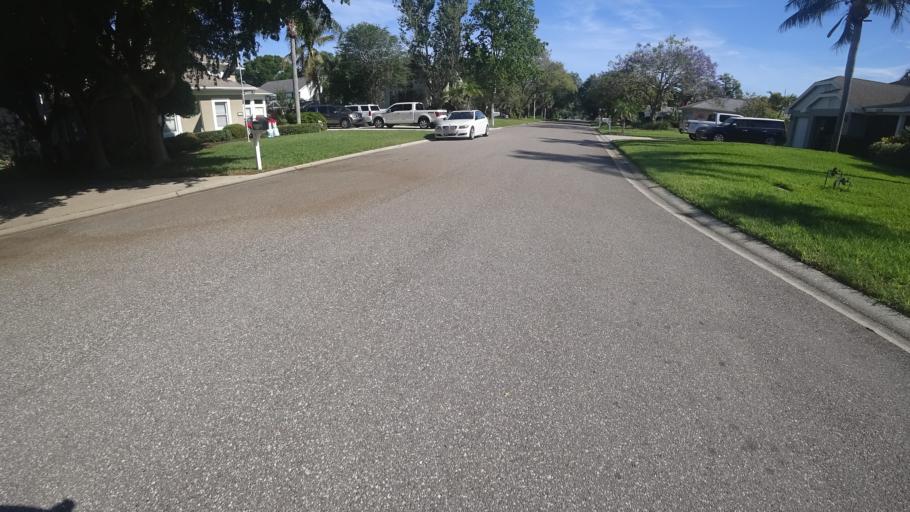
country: US
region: Florida
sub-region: Manatee County
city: West Bradenton
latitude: 27.5097
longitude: -82.6513
